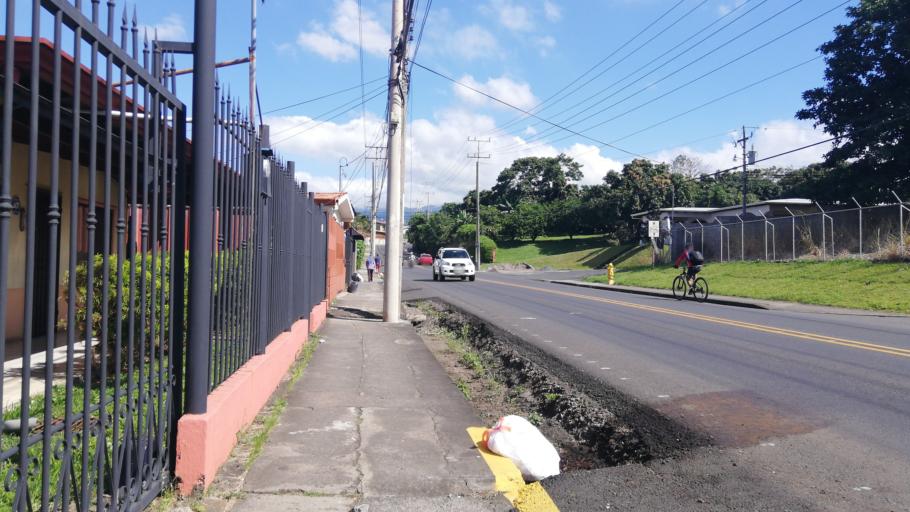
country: CR
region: Alajuela
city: San Juan
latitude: 10.0769
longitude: -84.3079
